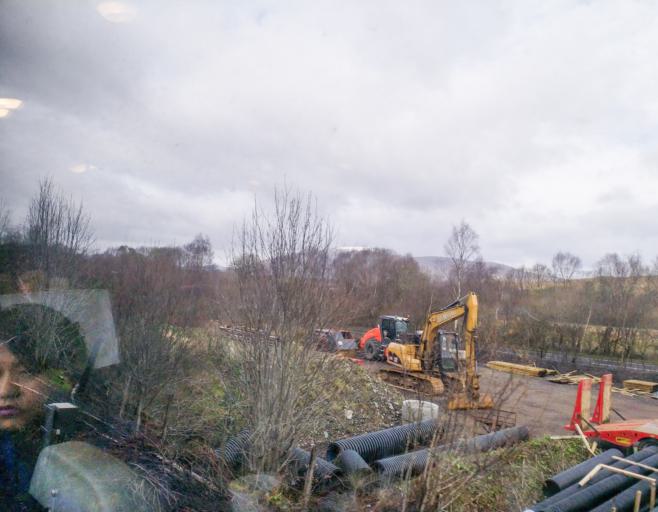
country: GB
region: Scotland
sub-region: Highland
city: Spean Bridge
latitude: 56.8888
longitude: -4.9320
